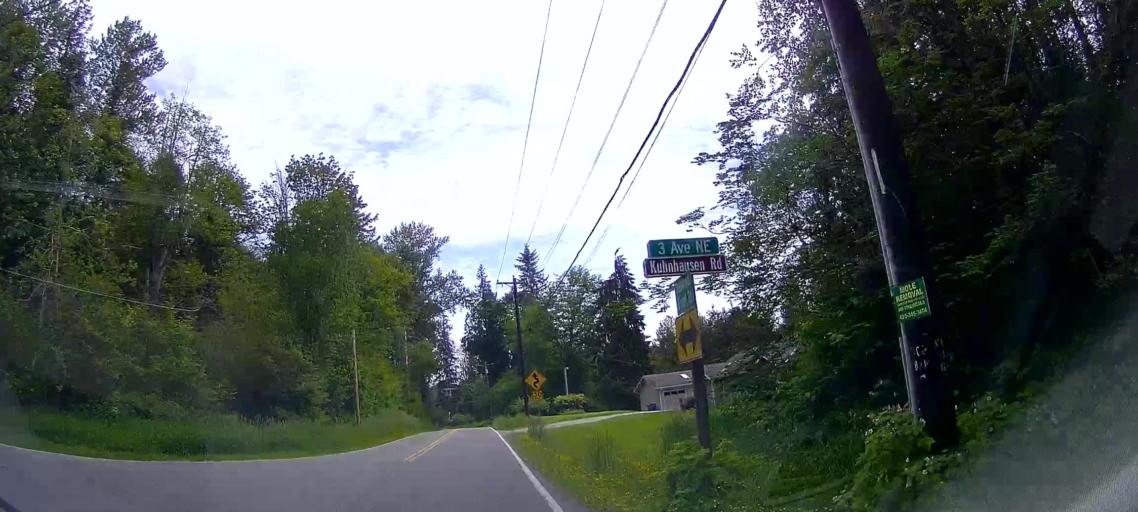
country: US
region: Washington
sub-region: Snohomish County
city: Bryant
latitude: 48.2388
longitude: -122.2263
